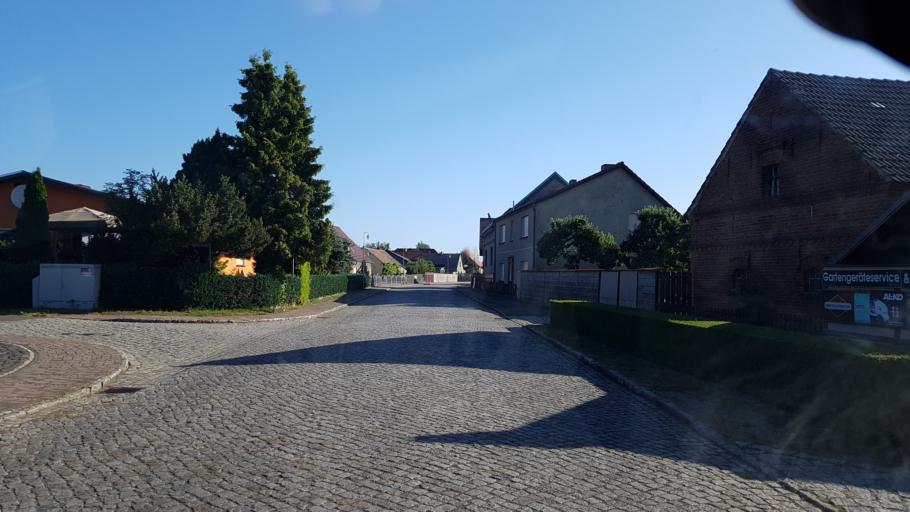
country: DE
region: Brandenburg
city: Kasel-Golzig
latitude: 51.9873
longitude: 13.6952
